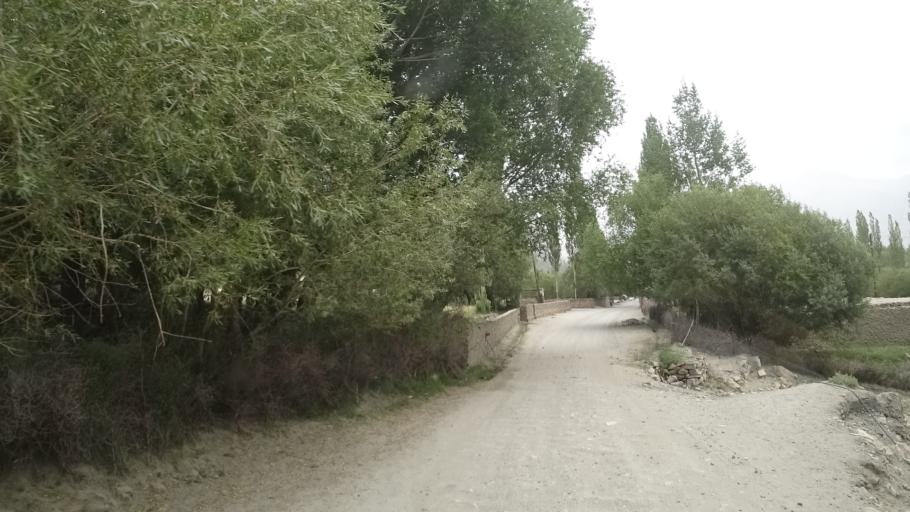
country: AF
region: Badakhshan
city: Khandud
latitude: 37.0291
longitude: 72.6160
